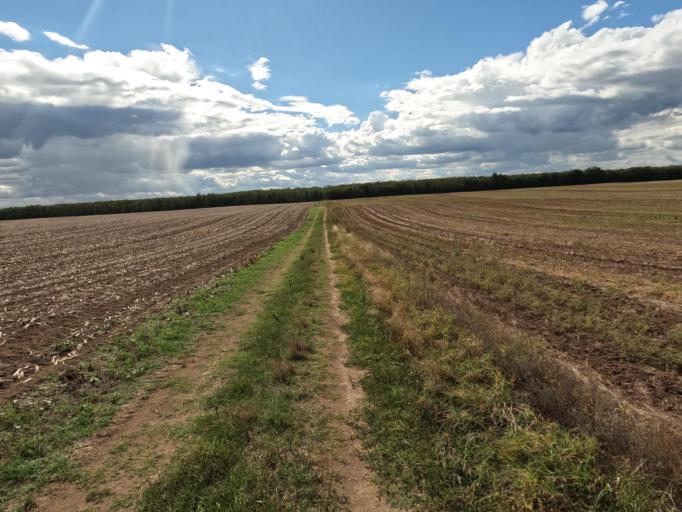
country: HU
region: Tolna
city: Tengelic
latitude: 46.5218
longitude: 18.6837
